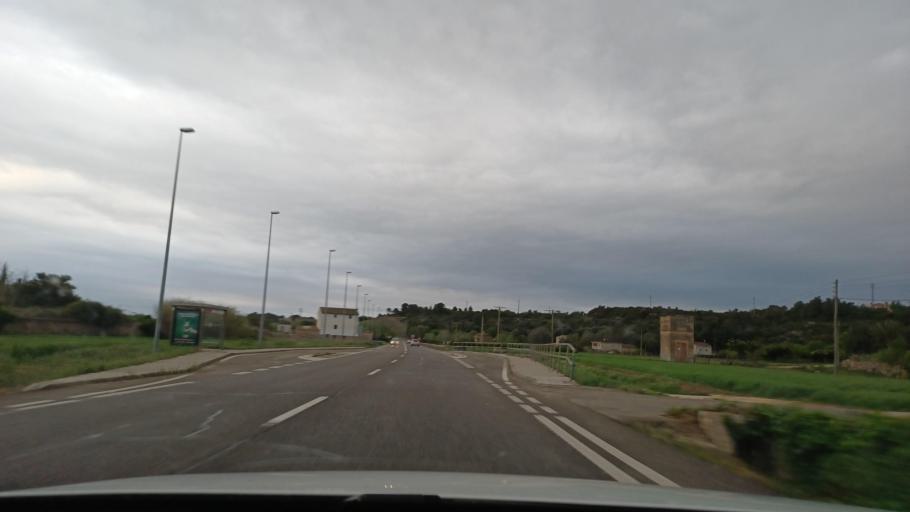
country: ES
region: Catalonia
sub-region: Provincia de Tarragona
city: Tortosa
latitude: 40.7804
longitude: 0.5050
